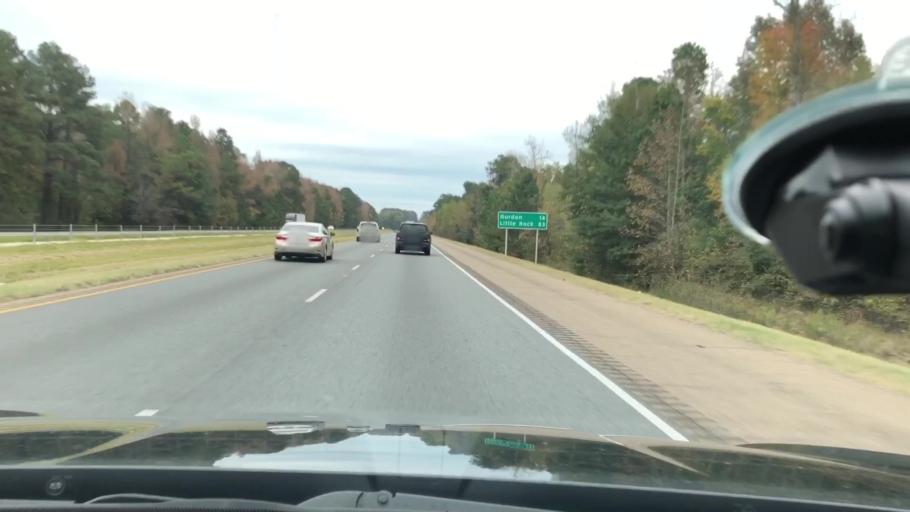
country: US
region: Arkansas
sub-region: Clark County
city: Gurdon
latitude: 33.9104
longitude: -93.2871
